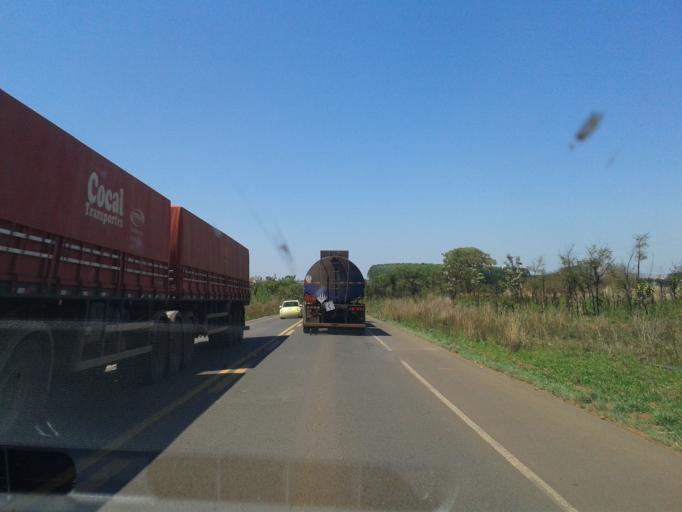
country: BR
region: Minas Gerais
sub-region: Araxa
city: Araxa
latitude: -19.3241
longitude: -47.3827
